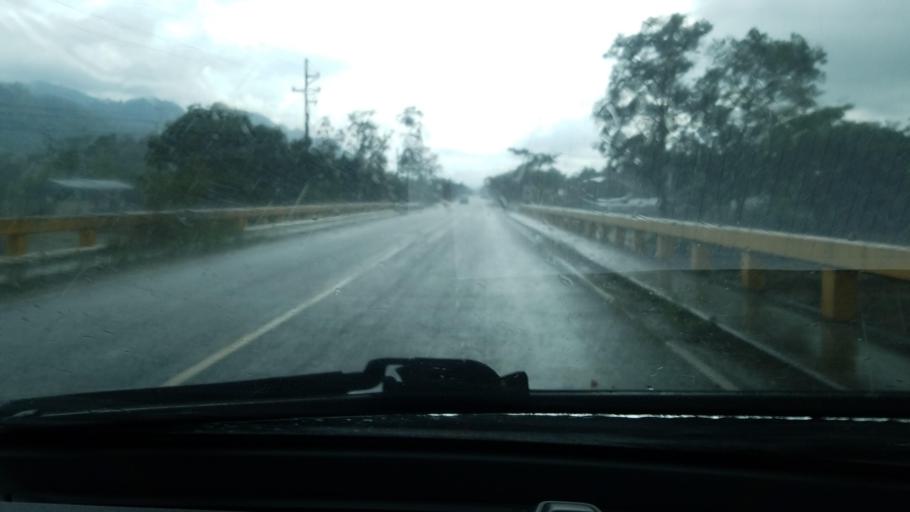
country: HN
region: Cortes
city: Rio Chiquito
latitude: 15.6300
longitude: -88.2506
